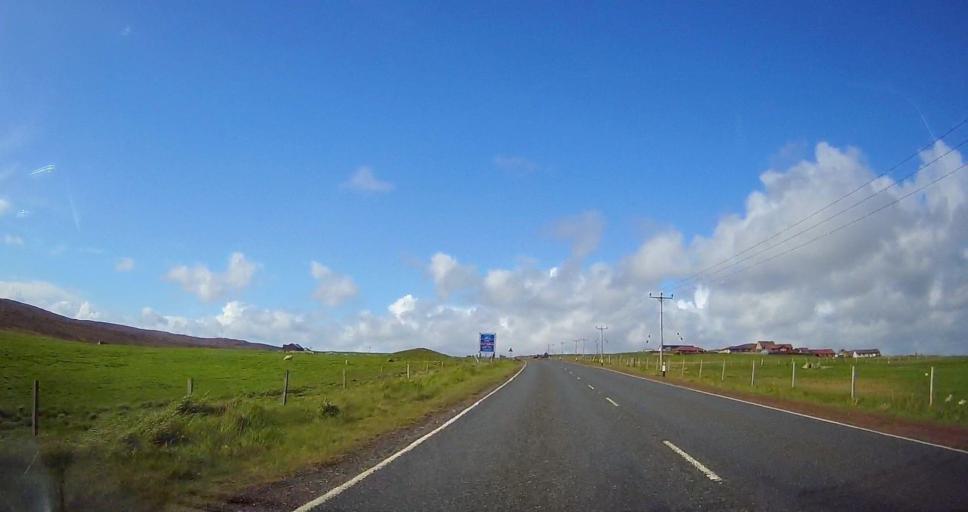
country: GB
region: Scotland
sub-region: Shetland Islands
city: Lerwick
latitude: 60.1957
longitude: -1.2320
